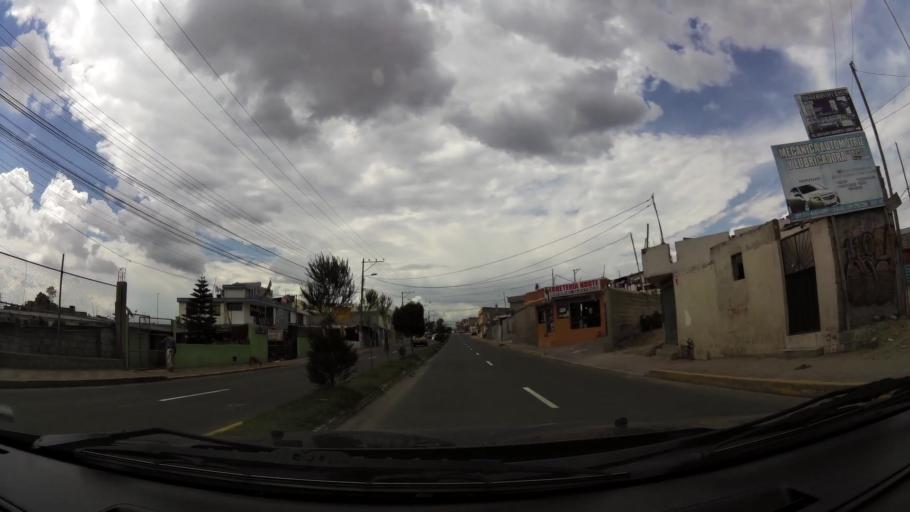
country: EC
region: Pichincha
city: Quito
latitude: -0.0990
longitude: -78.4446
